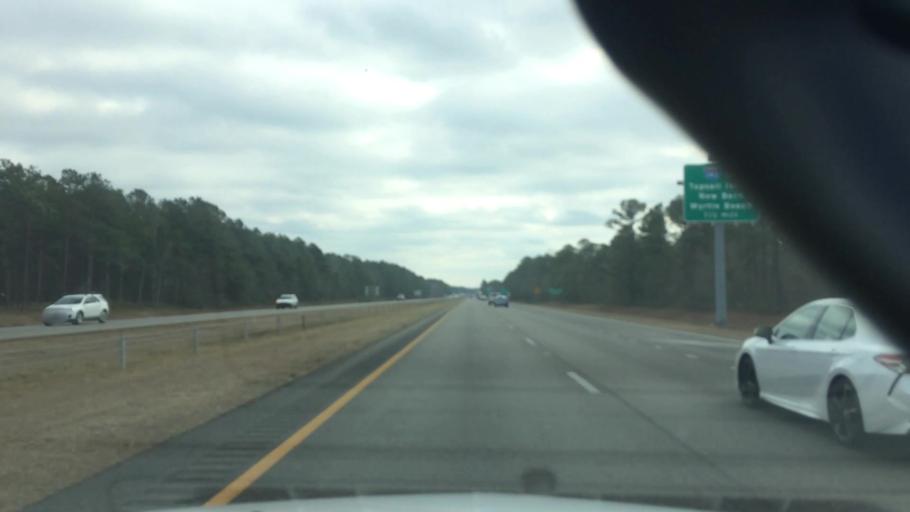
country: US
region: North Carolina
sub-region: New Hanover County
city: Castle Hayne
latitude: 34.3471
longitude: -77.8823
